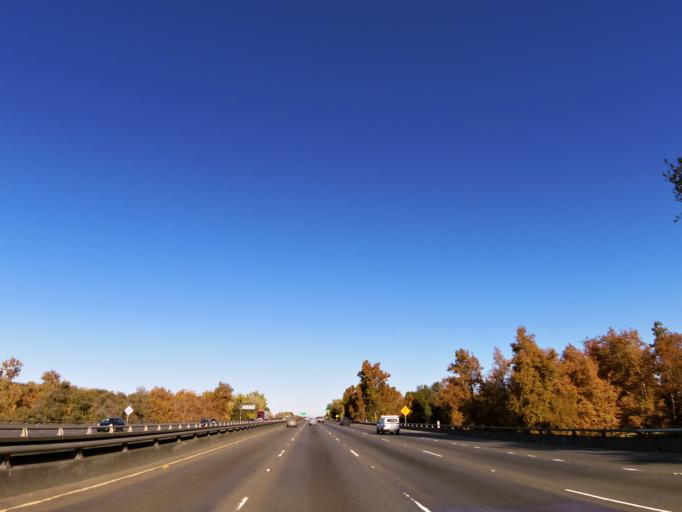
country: US
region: California
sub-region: Sacramento County
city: Sacramento
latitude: 38.6018
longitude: -121.5055
